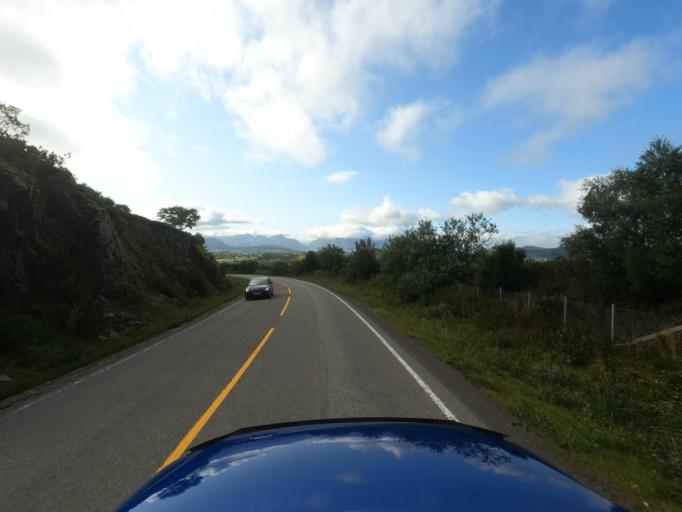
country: NO
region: Nordland
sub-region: Vestvagoy
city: Leknes
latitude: 68.1579
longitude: 13.6942
